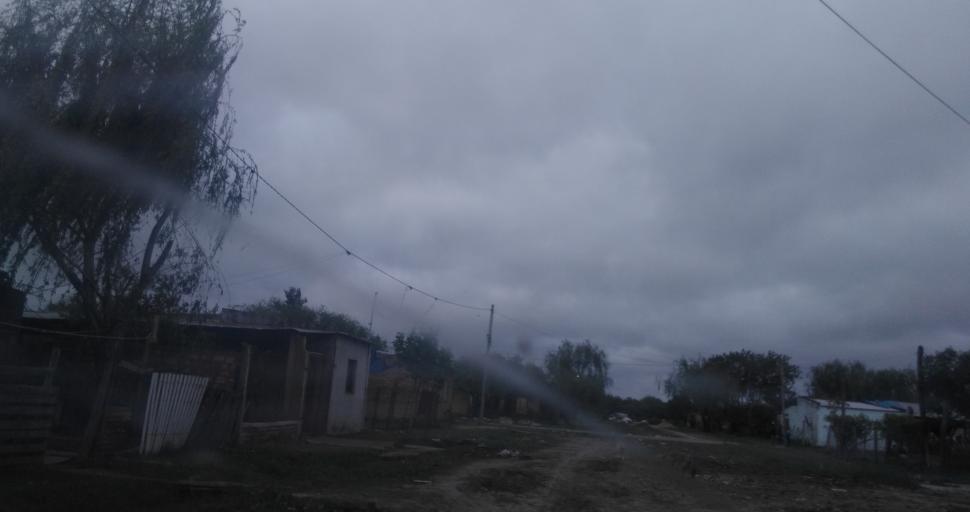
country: AR
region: Chaco
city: Resistencia
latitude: -27.4867
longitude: -59.0014
